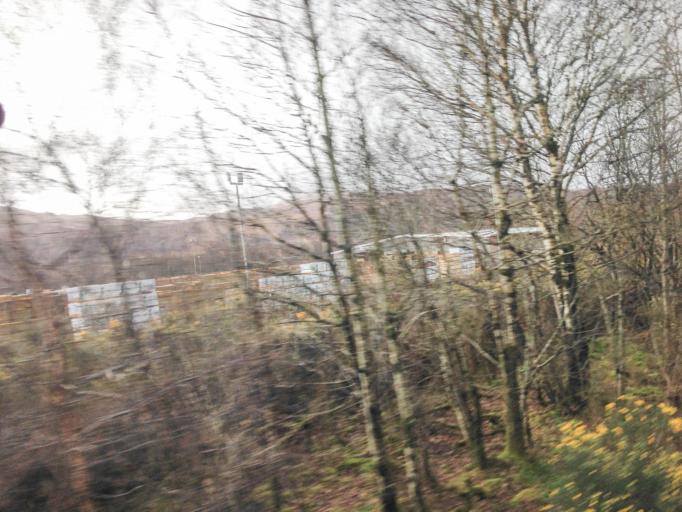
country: GB
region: Scotland
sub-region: Highland
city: Fort William
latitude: 56.8428
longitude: -5.1475
